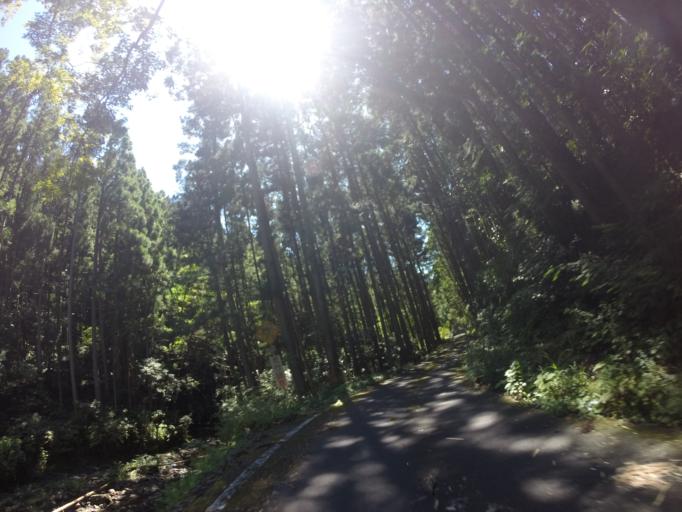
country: JP
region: Shizuoka
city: Kanaya
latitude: 34.9016
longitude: 138.1573
